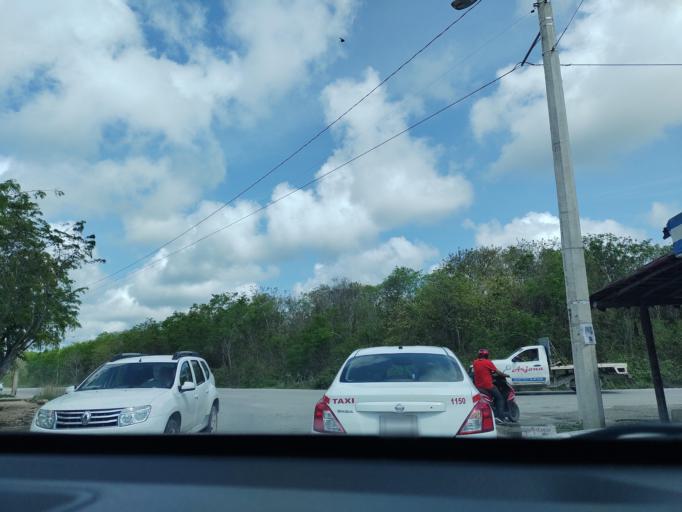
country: MX
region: Quintana Roo
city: Tulum
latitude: 20.2110
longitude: -87.4737
